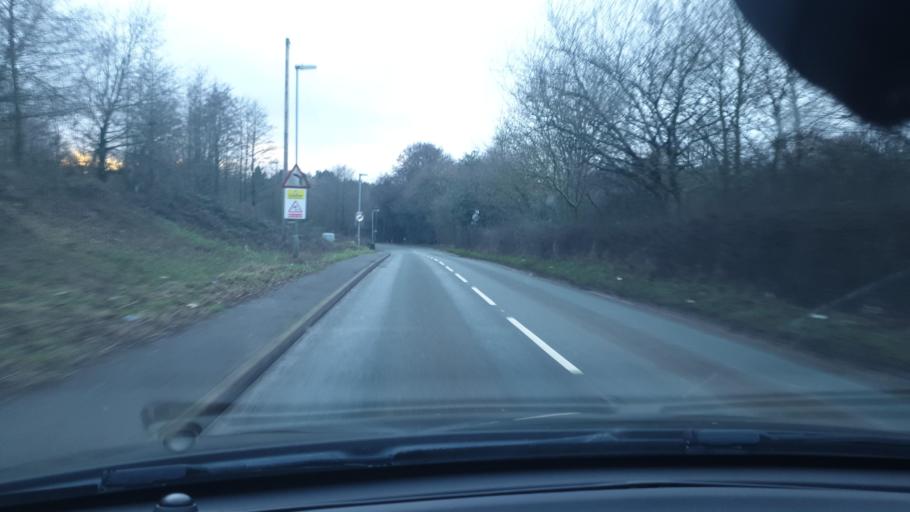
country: GB
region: England
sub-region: Staffordshire
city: Essington
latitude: 52.6573
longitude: -2.0486
